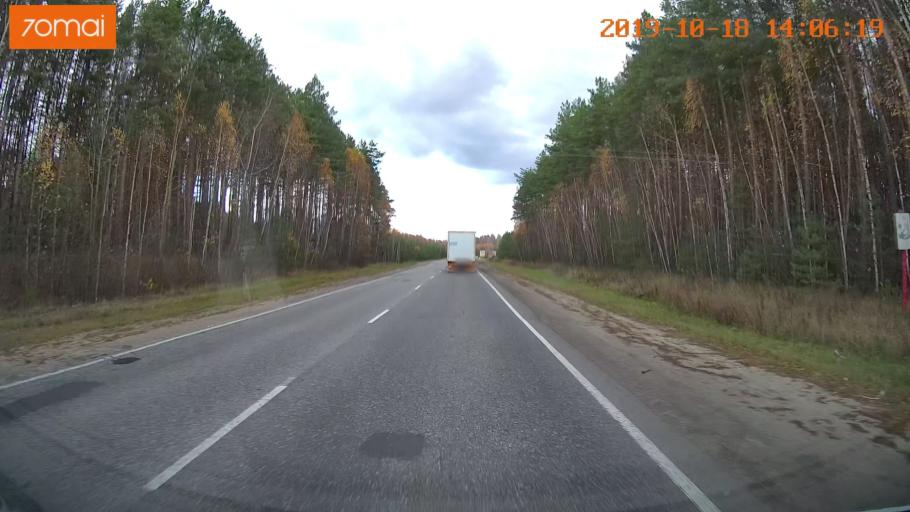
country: RU
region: Rjazan
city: Spas-Klepiki
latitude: 55.1439
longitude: 40.1497
